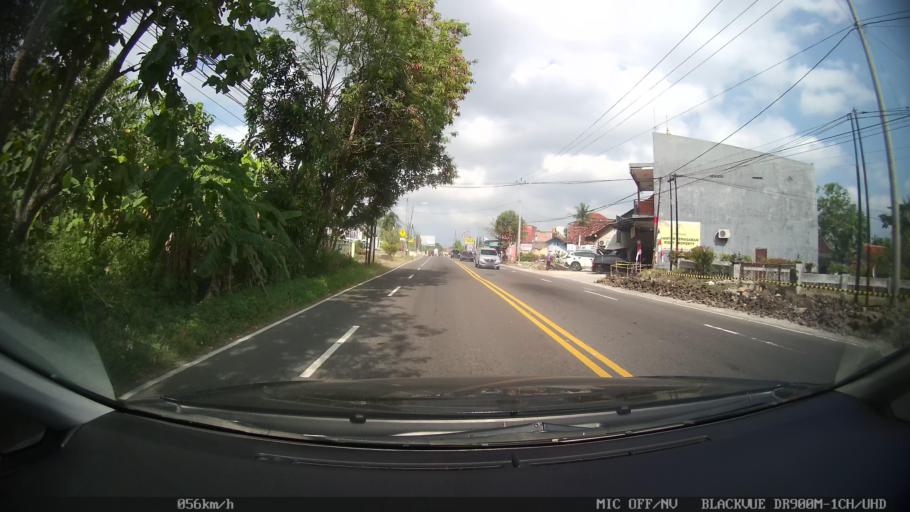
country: ID
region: Daerah Istimewa Yogyakarta
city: Srandakan
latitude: -7.8660
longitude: 110.1689
